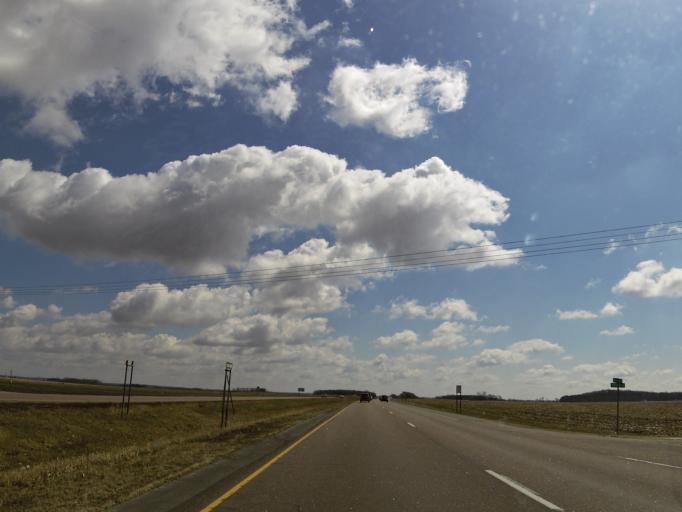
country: US
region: Minnesota
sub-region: Dakota County
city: Rosemount
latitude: 44.7029
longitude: -93.0281
